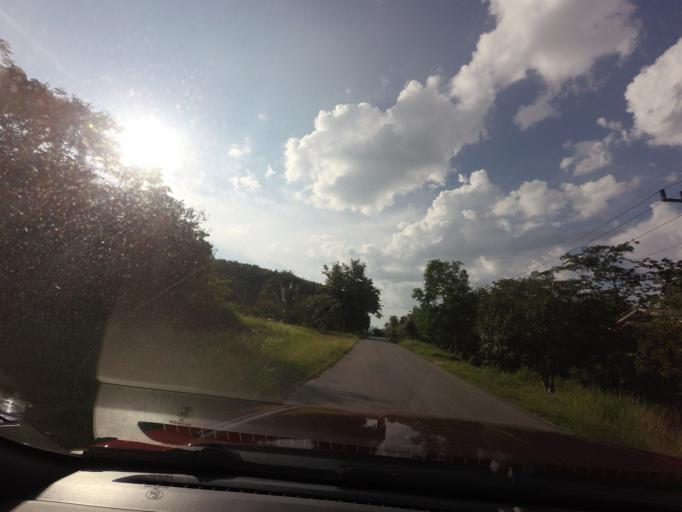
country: TH
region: Yala
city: Ban Nang Sata
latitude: 6.2146
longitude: 101.2325
